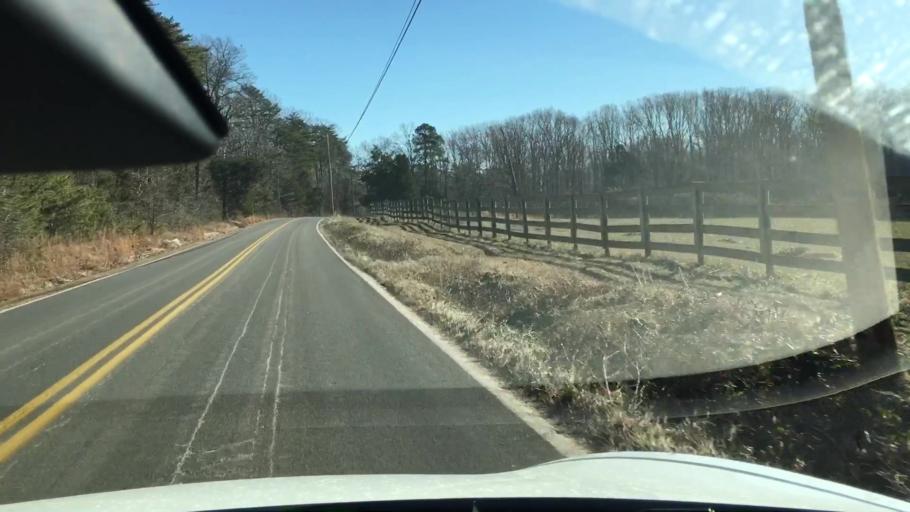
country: US
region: Virginia
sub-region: Henrico County
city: Short Pump
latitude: 37.5871
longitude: -77.7521
